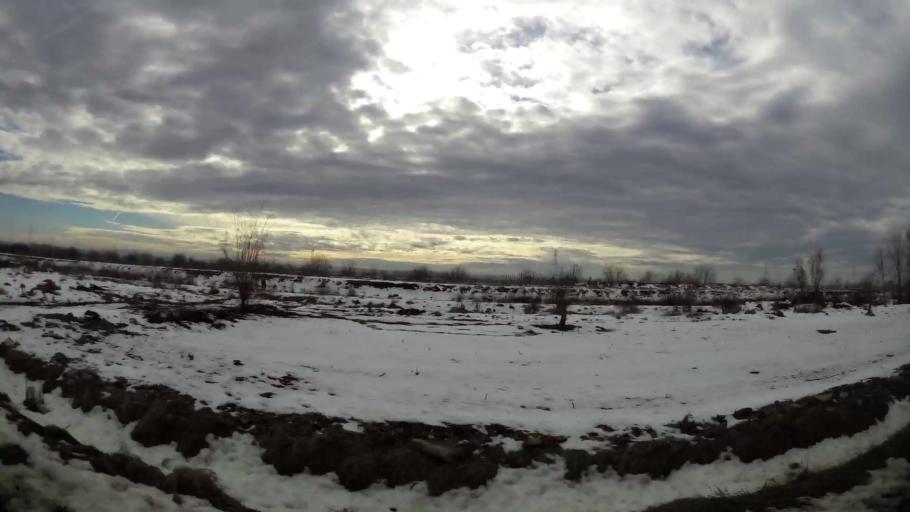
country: RS
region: Central Serbia
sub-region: Belgrade
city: Surcin
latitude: 44.7899
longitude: 20.2885
